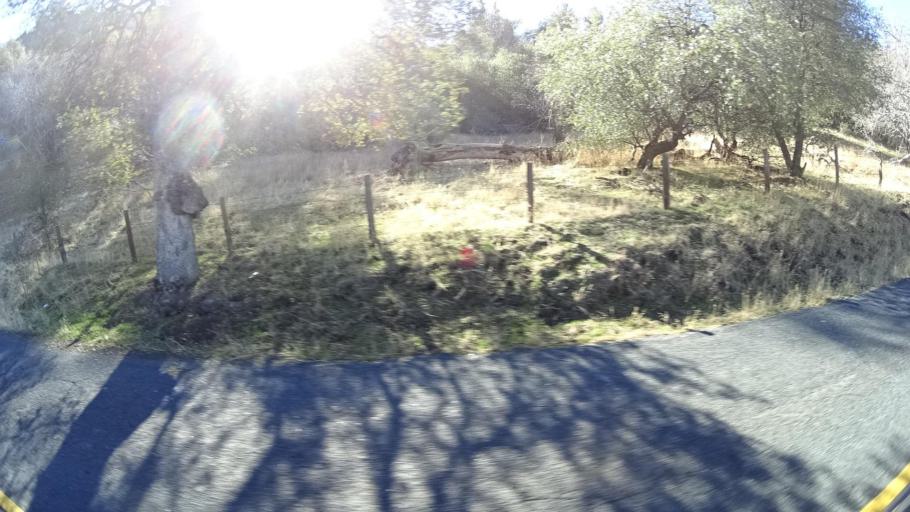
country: US
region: California
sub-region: Kern County
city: Alta Sierra
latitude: 35.7872
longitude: -118.7552
